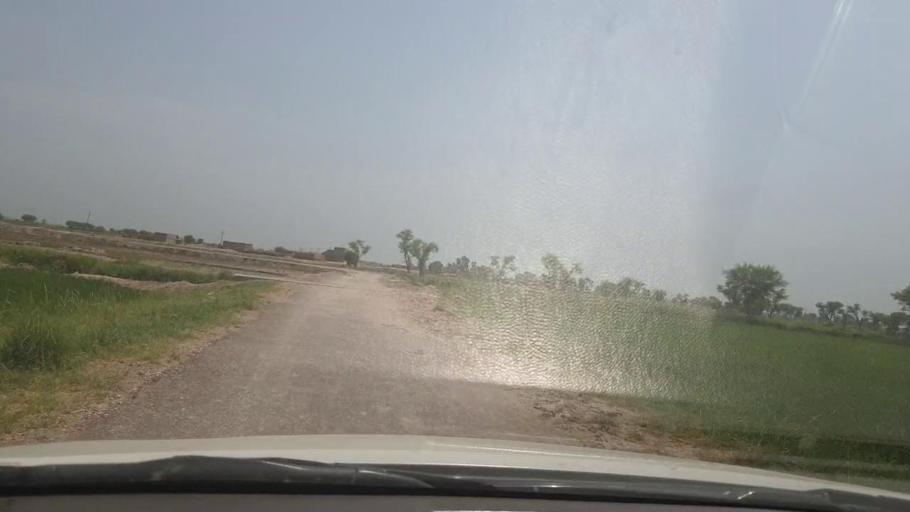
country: PK
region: Sindh
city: Shikarpur
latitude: 28.0434
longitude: 68.5722
